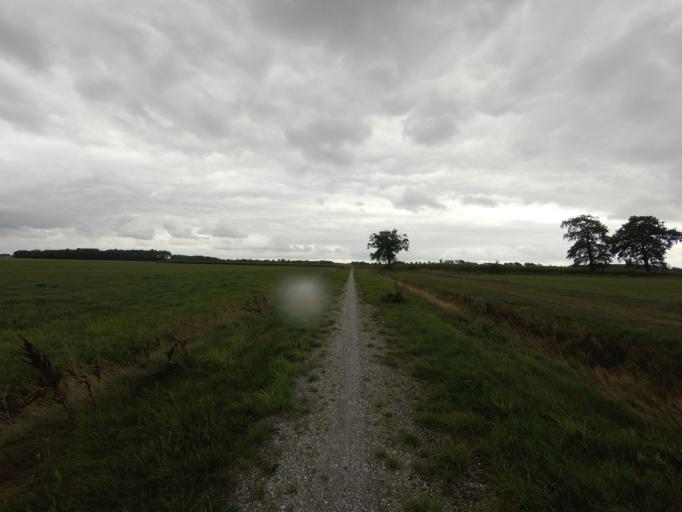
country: NL
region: Friesland
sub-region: Gemeente Weststellingwerf
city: Noordwolde
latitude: 52.9429
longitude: 6.1849
